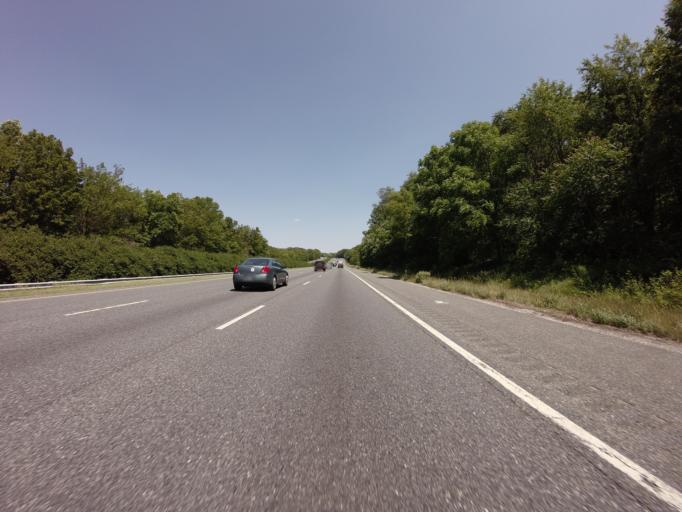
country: US
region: Maryland
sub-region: Carroll County
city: Mount Airy
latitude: 39.3507
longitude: -77.1114
